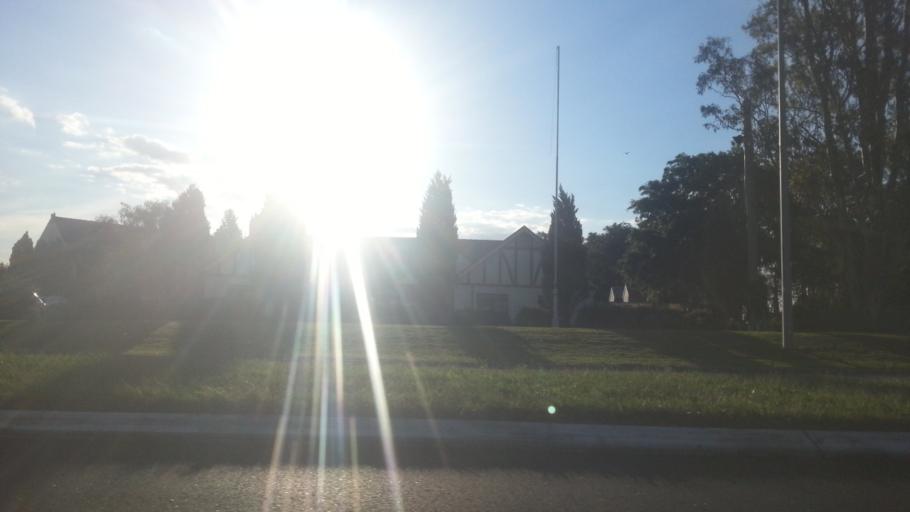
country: AU
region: New South Wales
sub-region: Camden
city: Camden South
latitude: -34.0921
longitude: 150.6950
